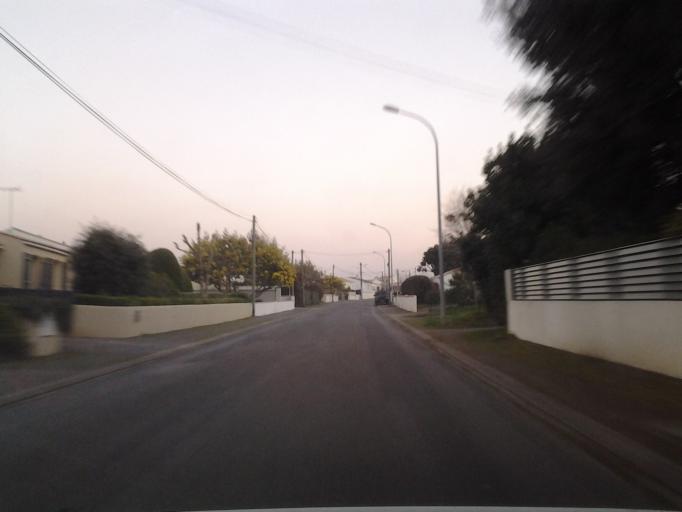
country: FR
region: Pays de la Loire
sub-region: Departement de la Vendee
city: Beauvoir-sur-Mer
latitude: 46.9115
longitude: -2.0394
